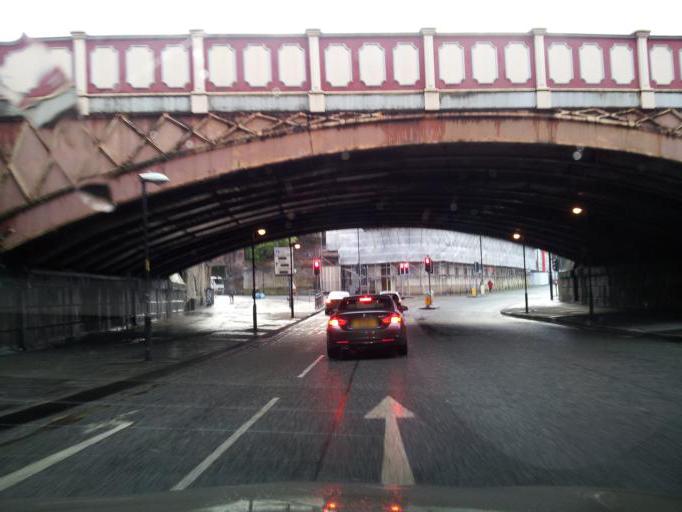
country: GB
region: England
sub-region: Manchester
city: Manchester
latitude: 53.4875
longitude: -2.2451
